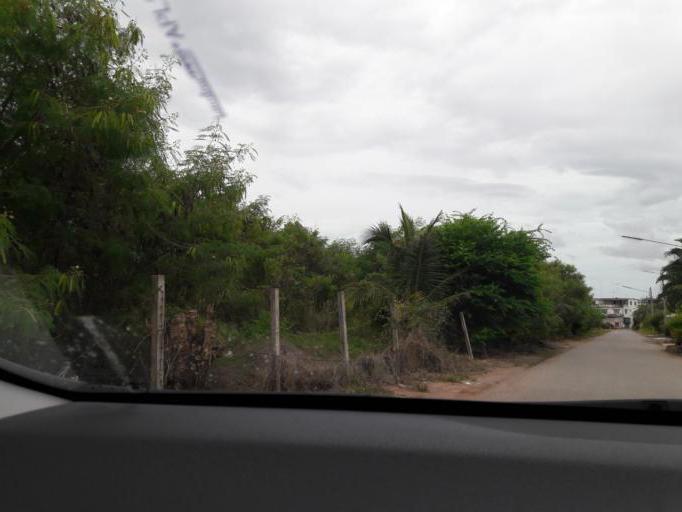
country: TH
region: Samut Sakhon
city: Ban Phaeo
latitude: 13.5543
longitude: 100.0372
